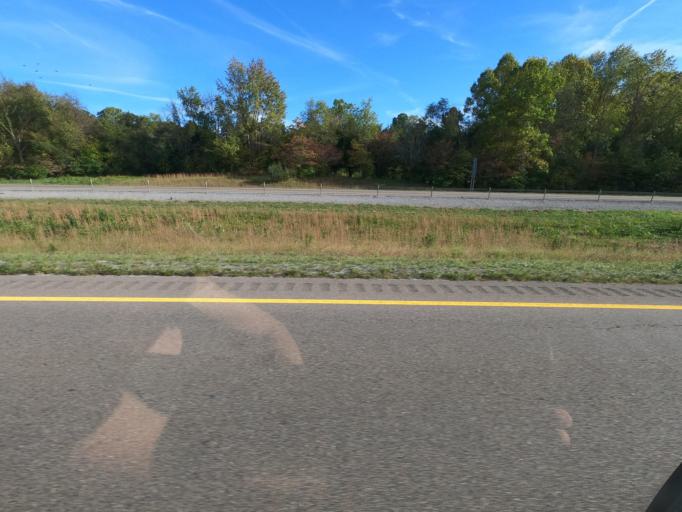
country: US
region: Tennessee
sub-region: Sullivan County
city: Colonial Heights
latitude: 36.4610
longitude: -82.5128
